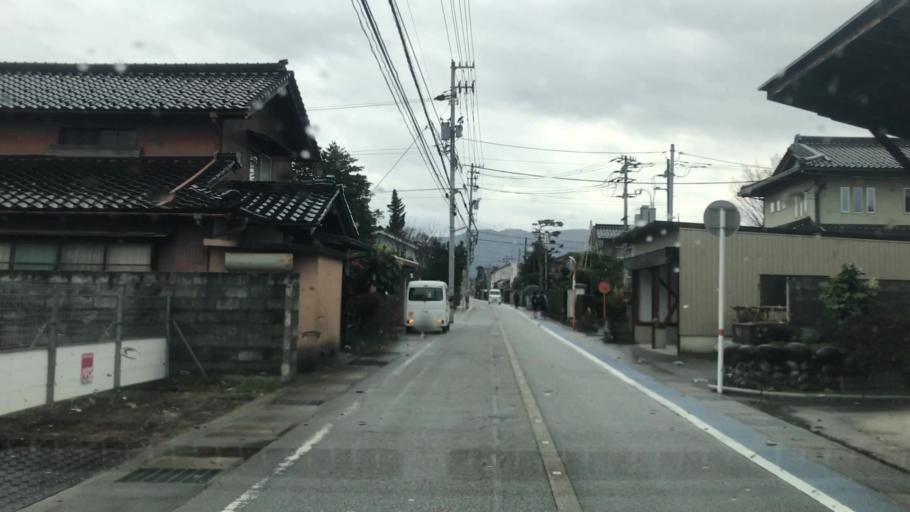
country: JP
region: Toyama
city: Yatsuomachi-higashikumisaka
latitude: 36.5962
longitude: 137.2063
